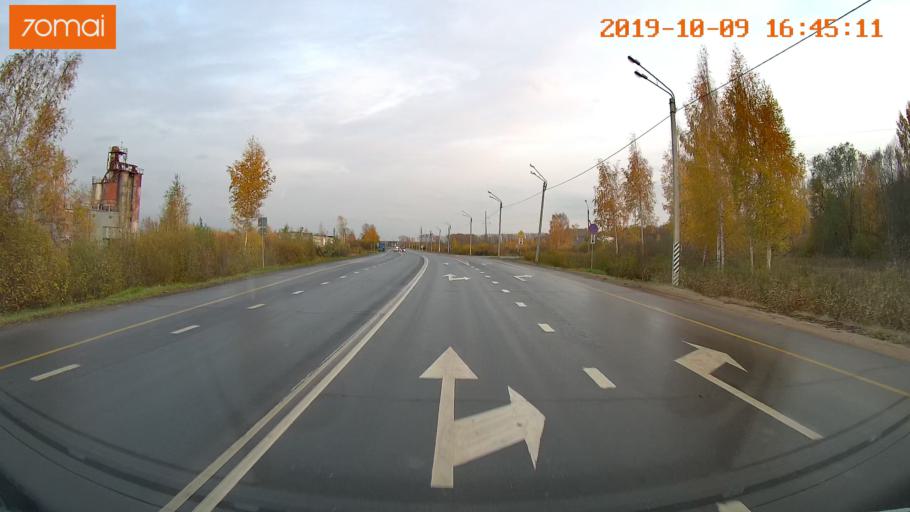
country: RU
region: Kostroma
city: Volgorechensk
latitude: 57.4477
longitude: 41.1510
